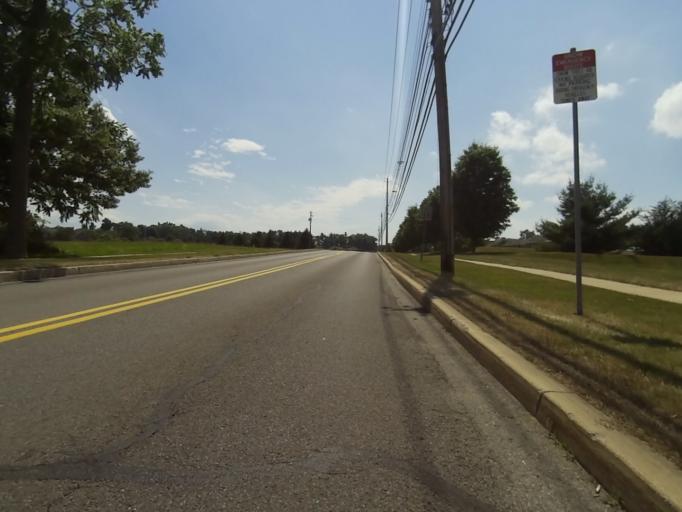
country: US
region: Pennsylvania
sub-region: Centre County
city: Park Forest Village
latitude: 40.7902
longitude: -77.9040
